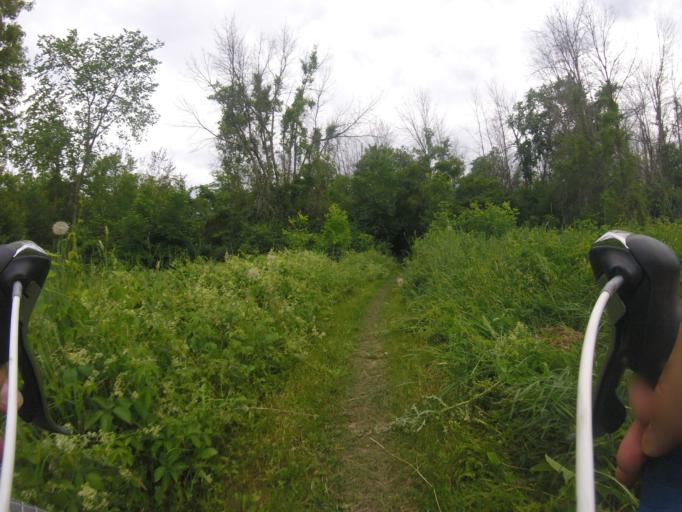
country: CA
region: Ontario
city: Bells Corners
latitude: 45.3317
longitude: -75.7982
